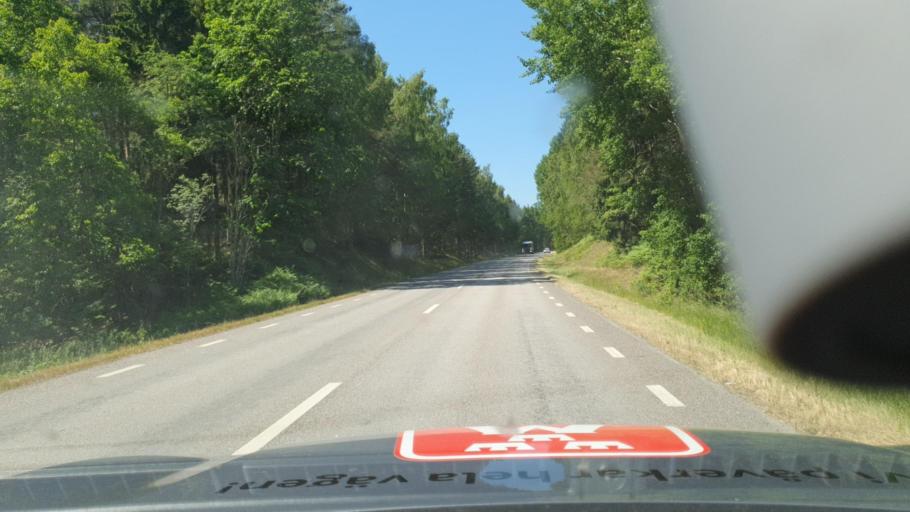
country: SE
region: Kalmar
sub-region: Torsas Kommun
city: Torsas
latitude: 56.4064
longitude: 16.0264
